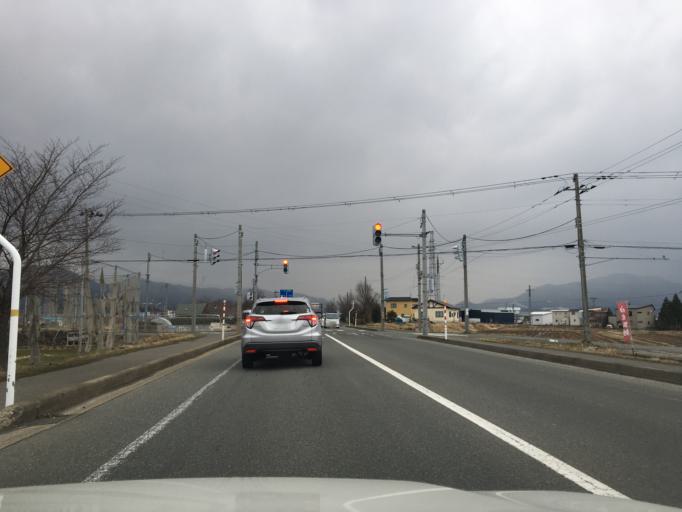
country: JP
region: Aomori
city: Kuroishi
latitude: 40.5759
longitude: 140.5683
